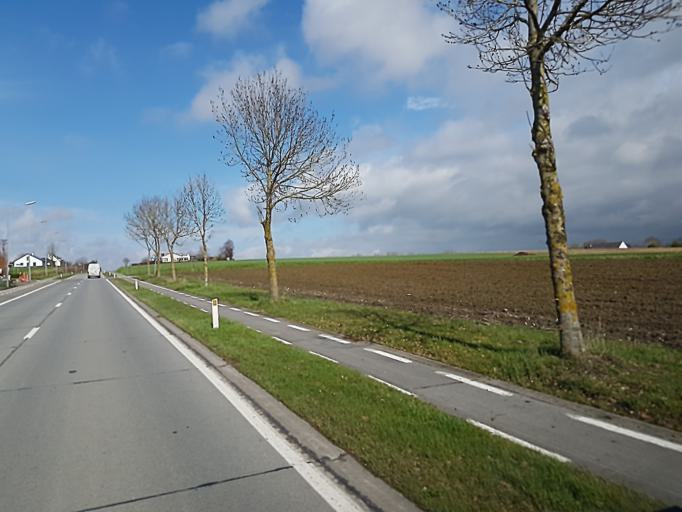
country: BE
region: Flanders
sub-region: Provincie Oost-Vlaanderen
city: Oudenaarde
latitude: 50.8644
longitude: 3.5686
